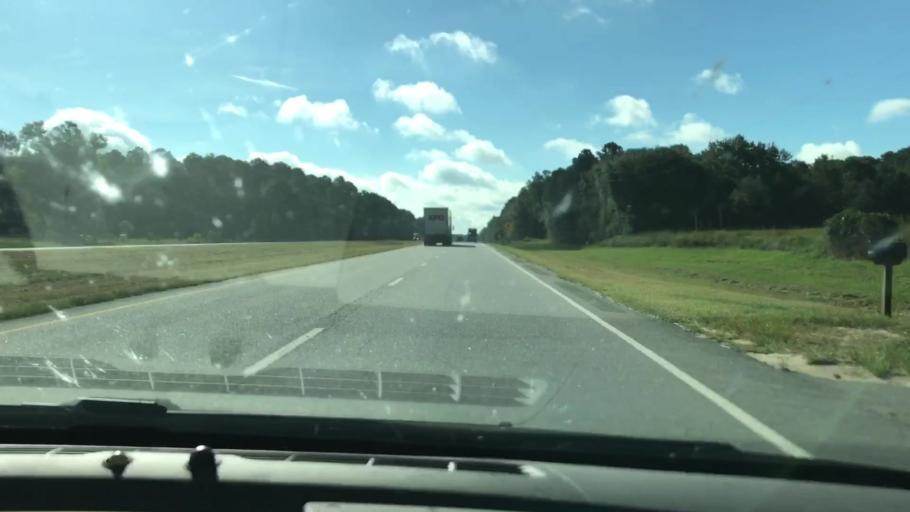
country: US
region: Georgia
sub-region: Dougherty County
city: Albany
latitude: 31.5677
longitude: -84.0204
